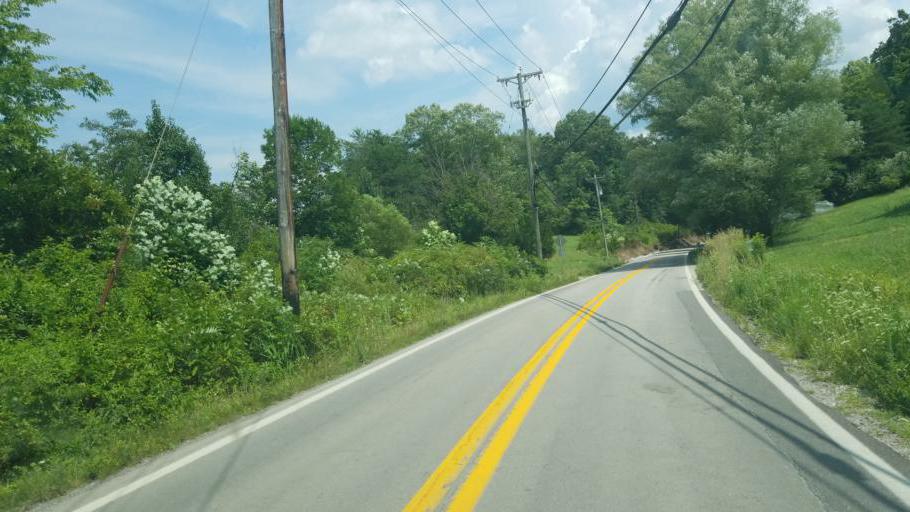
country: US
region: West Virginia
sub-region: Putnam County
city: Teays Valley
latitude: 38.4555
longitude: -81.8866
